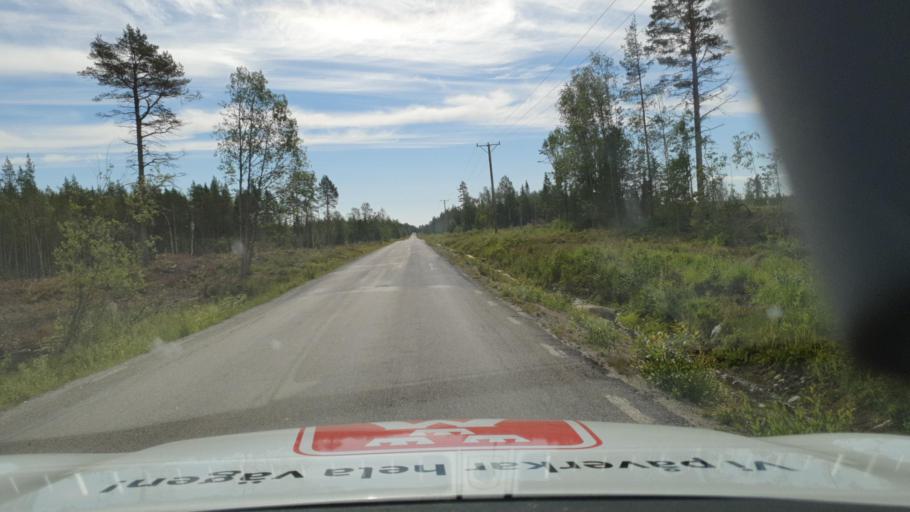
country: SE
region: Vaesterbotten
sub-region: Umea Kommun
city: Saevar
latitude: 63.8724
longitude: 20.7126
